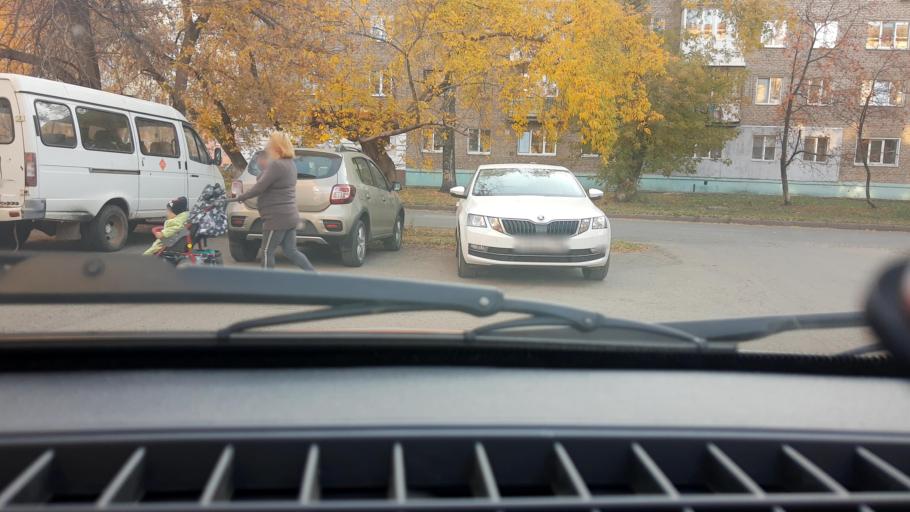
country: RU
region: Bashkortostan
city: Mikhaylovka
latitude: 54.7060
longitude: 55.8331
